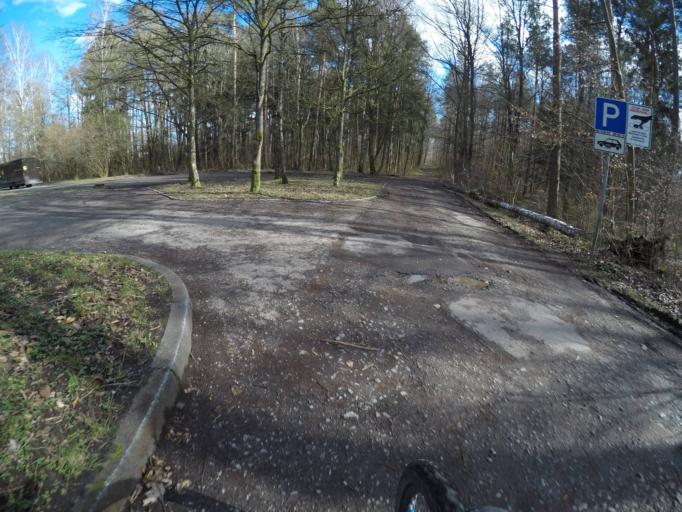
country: DE
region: Baden-Wuerttemberg
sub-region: Regierungsbezirk Stuttgart
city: Leinfelden-Echterdingen
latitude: 48.6791
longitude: 9.1506
